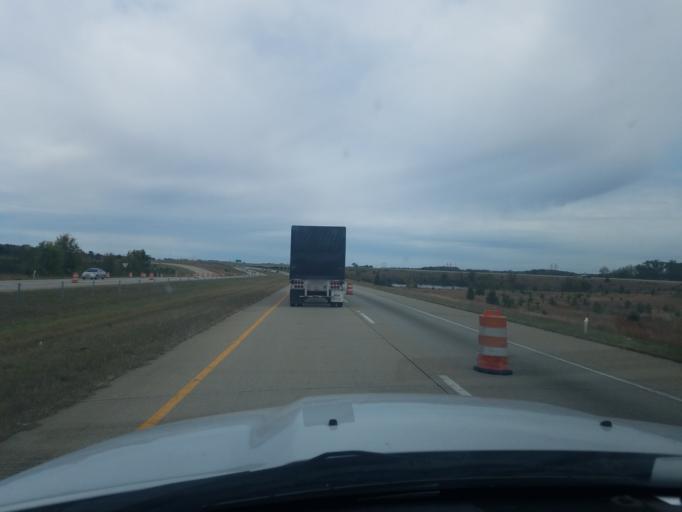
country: US
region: Indiana
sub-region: Vanderburgh County
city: Darmstadt
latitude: 38.1303
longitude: -87.4743
